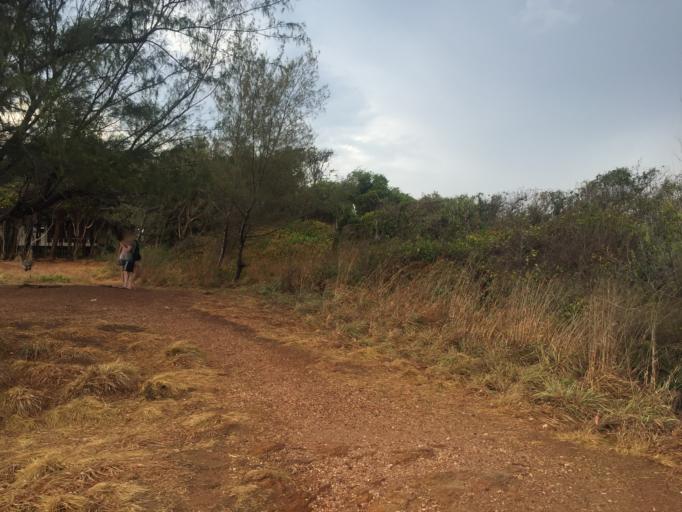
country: TH
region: Rayong
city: Rayong
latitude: 12.5226
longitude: 101.4447
